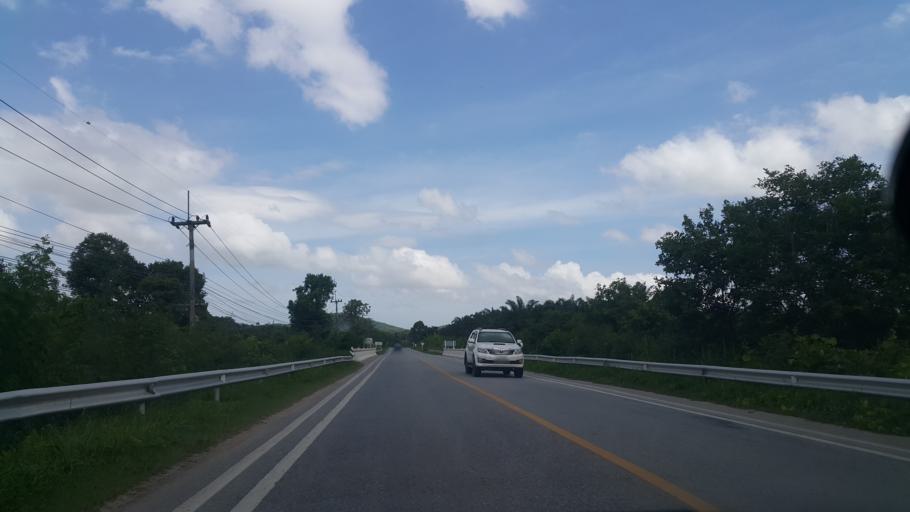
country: TH
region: Rayong
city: Ban Chang
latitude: 12.8183
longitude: 101.0594
